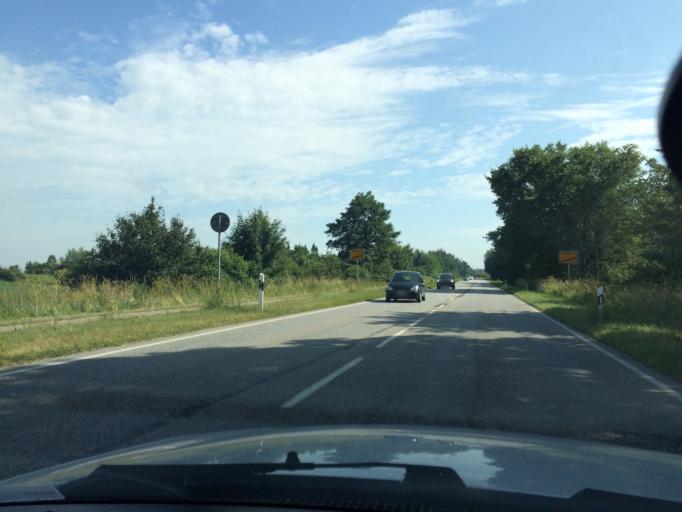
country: DE
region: Schleswig-Holstein
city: Jarplund-Weding
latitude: 54.7359
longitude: 9.4415
